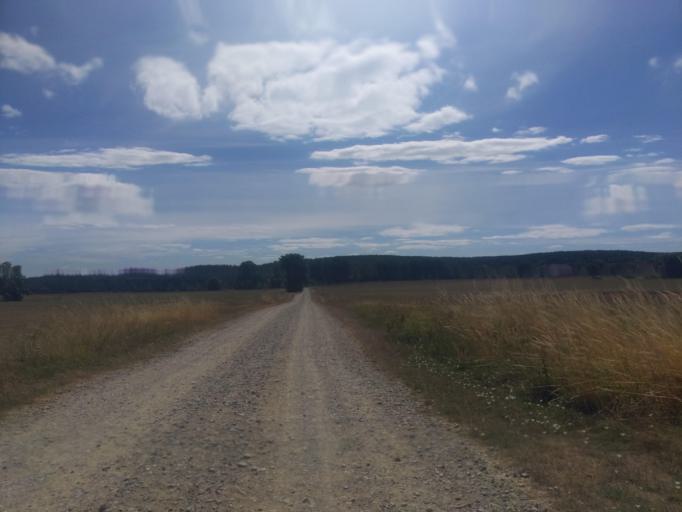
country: DE
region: Lower Saxony
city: Neu Darchau
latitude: 53.2464
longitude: 10.8525
